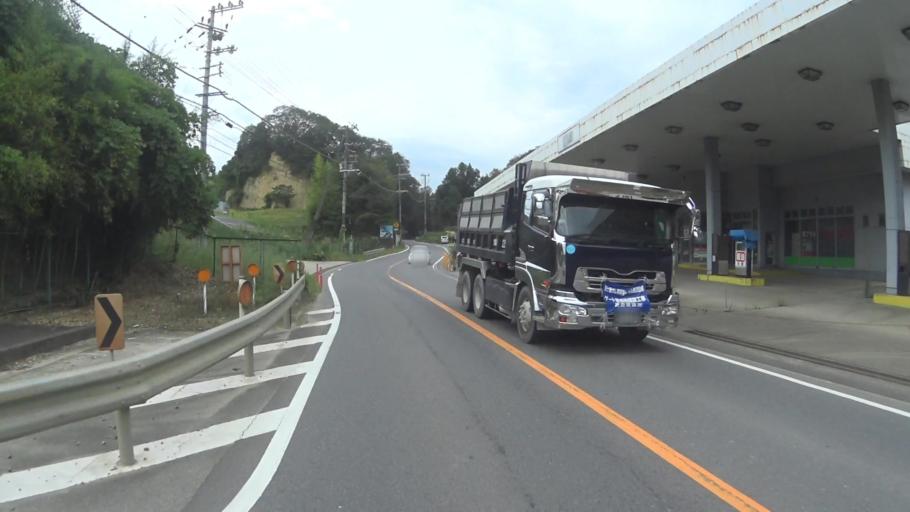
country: JP
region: Kyoto
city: Uji
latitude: 34.8389
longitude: 135.8310
